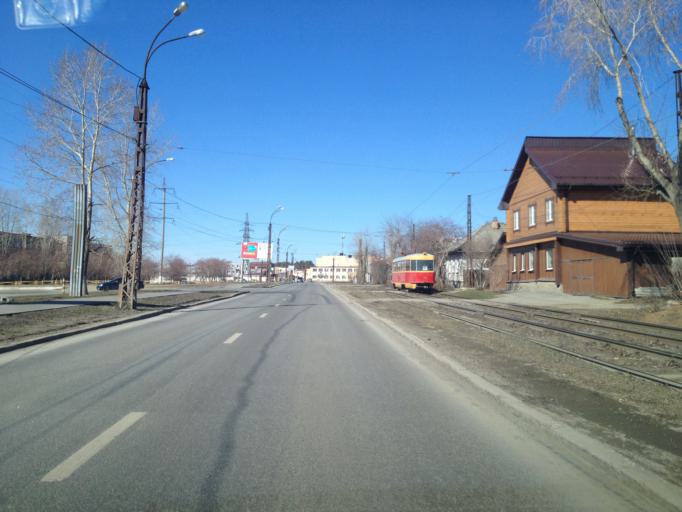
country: RU
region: Sverdlovsk
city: Sovkhoznyy
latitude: 56.7570
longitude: 60.5924
